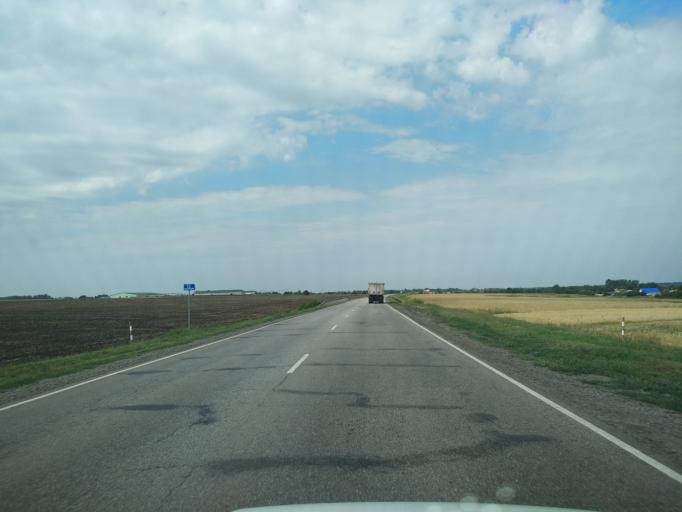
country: RU
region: Voronezj
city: Verkhnyaya Khava
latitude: 51.6792
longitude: 39.8901
